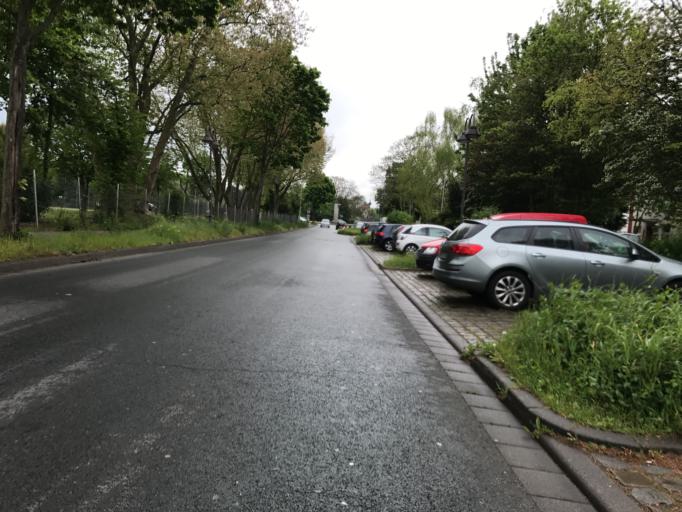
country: DE
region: Rheinland-Pfalz
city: Mainz
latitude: 49.9867
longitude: 8.2637
